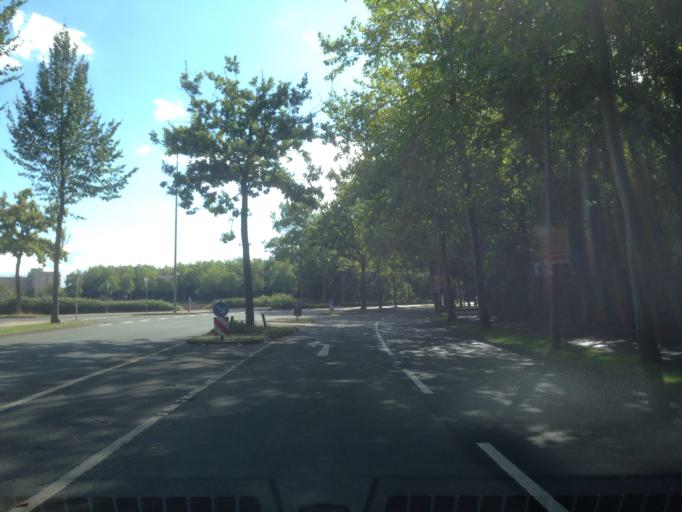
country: DE
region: North Rhine-Westphalia
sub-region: Regierungsbezirk Munster
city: Muenster
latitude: 51.9642
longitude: 7.5888
